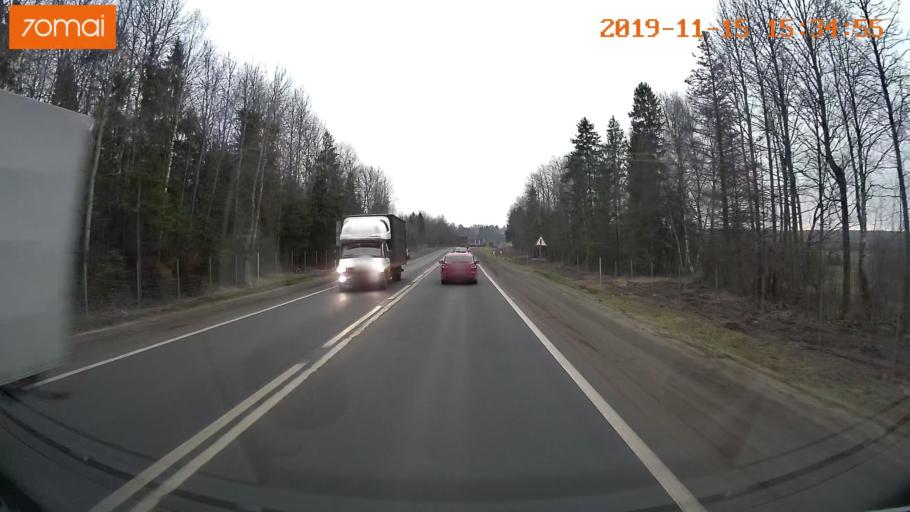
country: RU
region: Jaroslavl
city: Danilov
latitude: 58.0646
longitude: 40.0881
